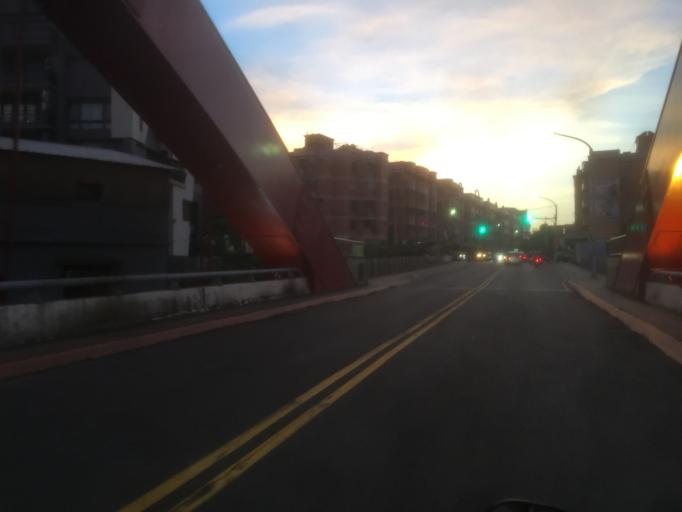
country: TW
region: Taiwan
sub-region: Hsinchu
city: Hsinchu
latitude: 24.7935
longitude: 120.9610
